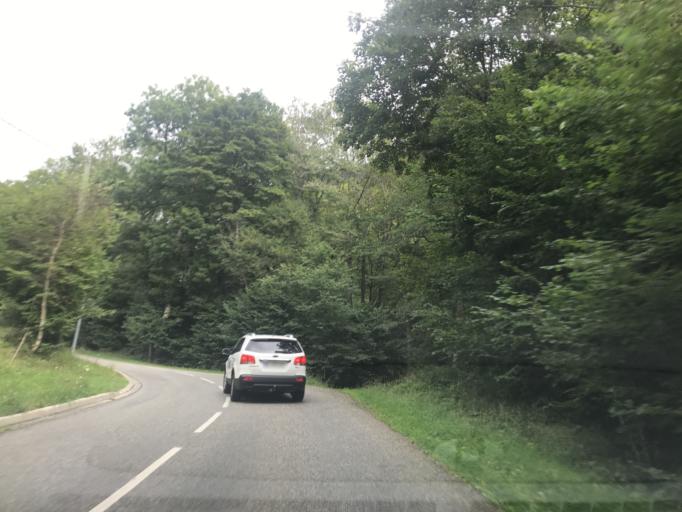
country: FR
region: Midi-Pyrenees
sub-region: Departement de la Haute-Garonne
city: Bagneres-de-Luchon
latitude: 42.7686
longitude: 0.6455
